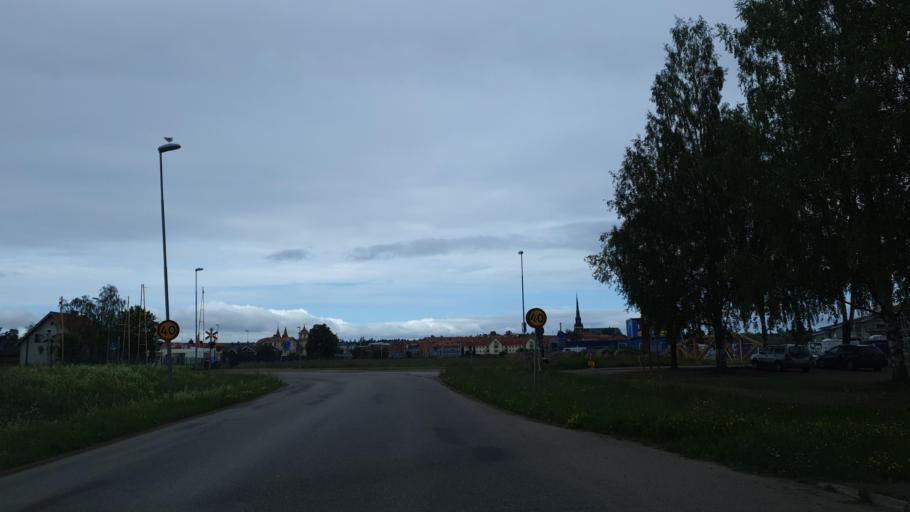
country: SE
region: Dalarna
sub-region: Mora Kommun
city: Mora
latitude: 60.9995
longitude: 14.5415
